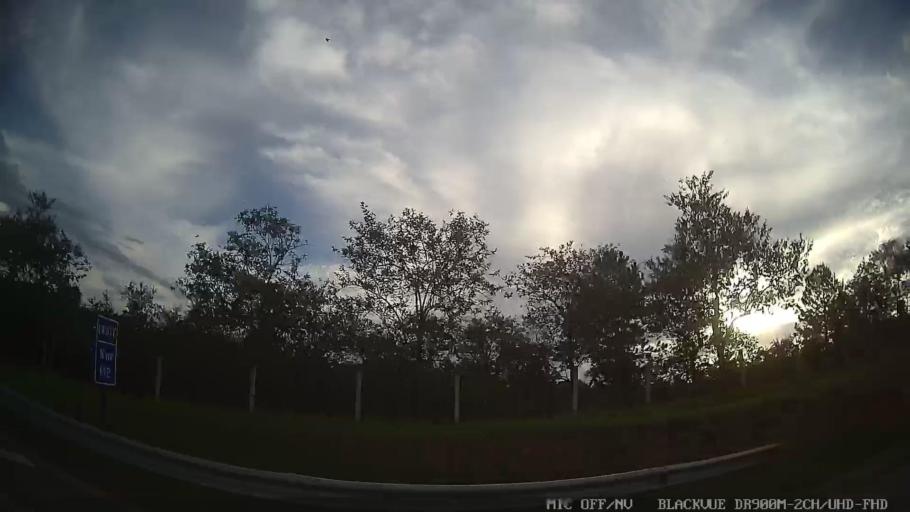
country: BR
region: Sao Paulo
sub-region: Porto Feliz
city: Porto Feliz
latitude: -23.2078
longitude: -47.5968
